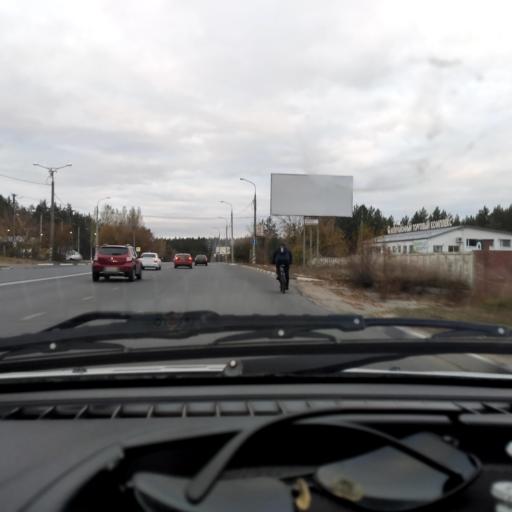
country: RU
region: Samara
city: Zhigulevsk
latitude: 53.4975
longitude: 49.4732
